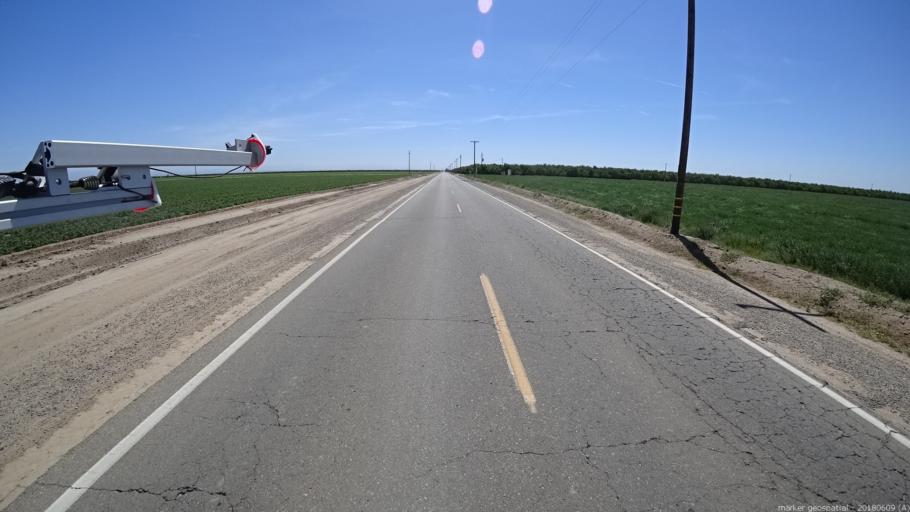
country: US
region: California
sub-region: Madera County
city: Fairmead
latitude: 36.9528
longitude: -120.2312
